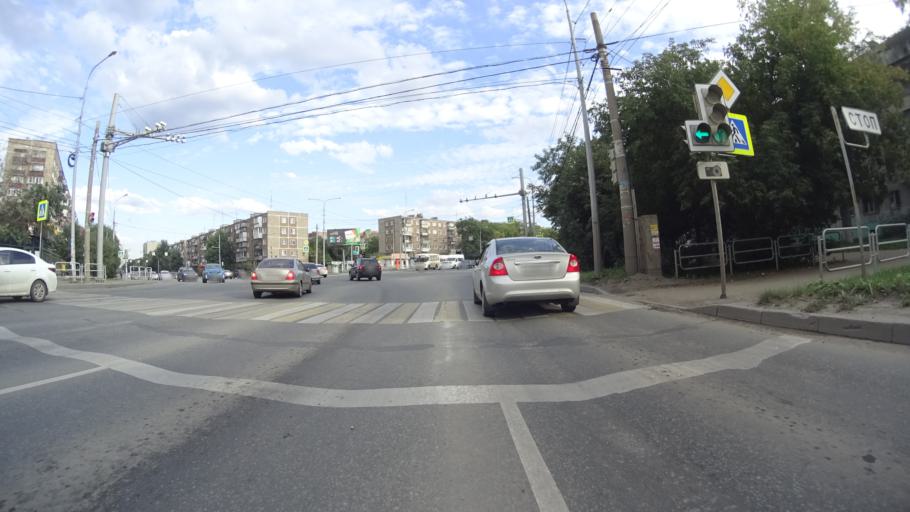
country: RU
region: Chelyabinsk
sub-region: Gorod Chelyabinsk
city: Chelyabinsk
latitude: 55.1988
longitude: 61.3314
